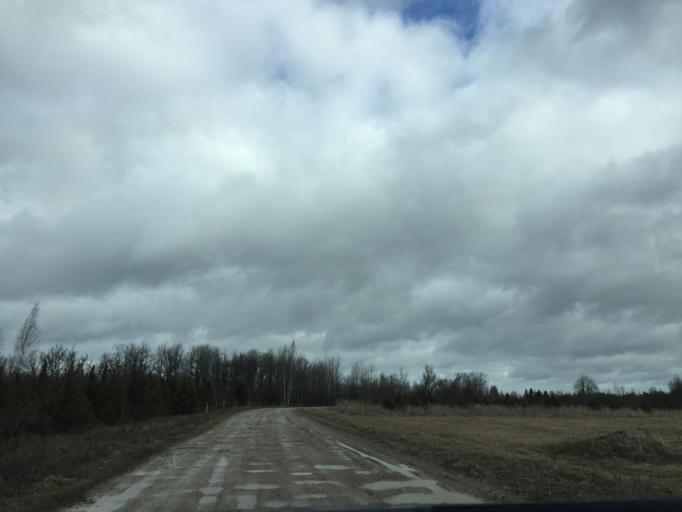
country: EE
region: Laeaene
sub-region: Haapsalu linn
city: Haapsalu
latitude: 58.6829
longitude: 23.5419
